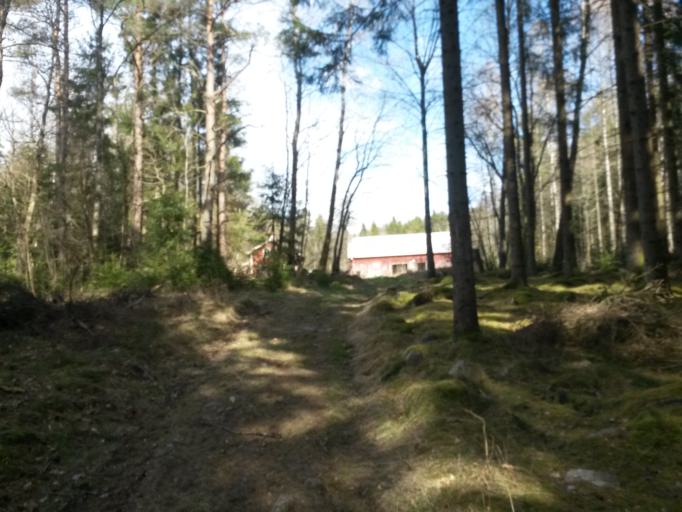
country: SE
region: Vaestra Goetaland
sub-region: Vargarda Kommun
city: Jonstorp
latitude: 57.9547
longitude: 12.6896
